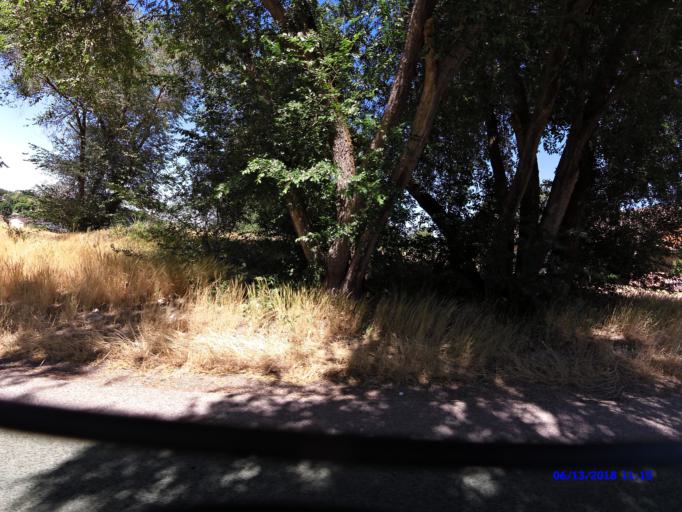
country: US
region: Utah
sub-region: Weber County
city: South Ogden
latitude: 41.2082
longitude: -111.9500
